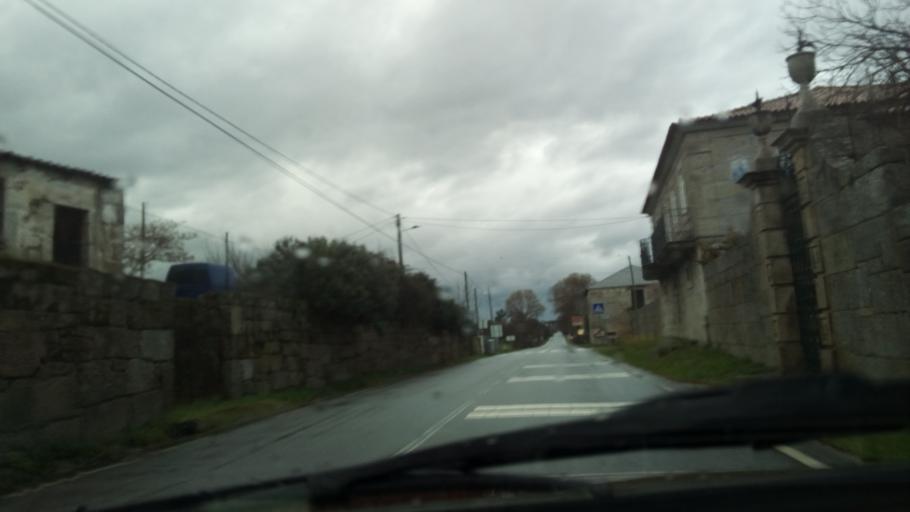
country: PT
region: Guarda
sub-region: Celorico da Beira
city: Celorico da Beira
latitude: 40.6188
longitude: -7.3114
